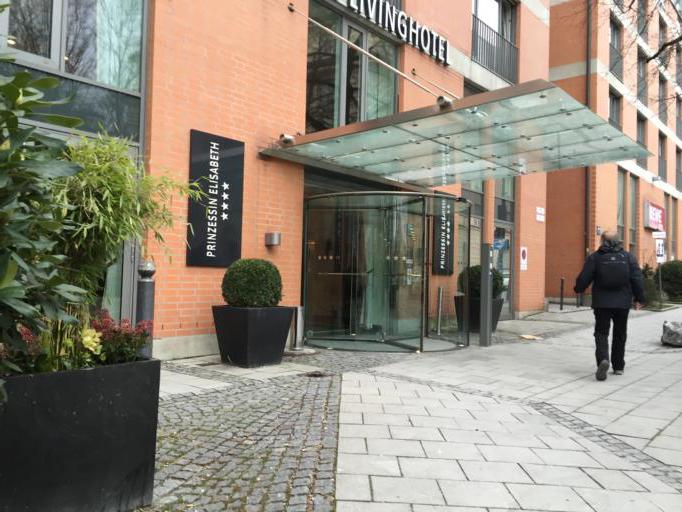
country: DE
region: Bavaria
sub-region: Upper Bavaria
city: Munich
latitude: 48.1226
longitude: 11.5650
